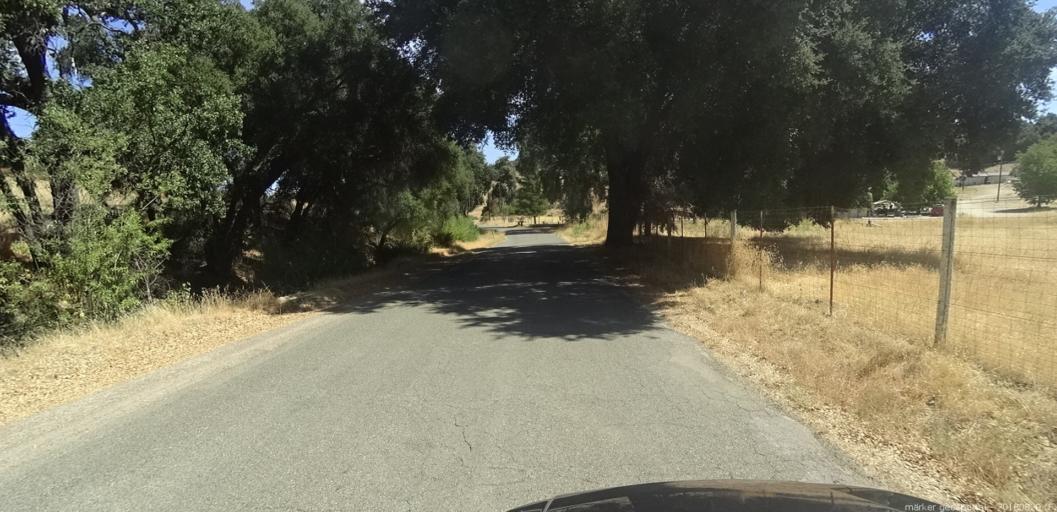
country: US
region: California
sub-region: San Luis Obispo County
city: Lake Nacimiento
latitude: 35.8364
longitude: -121.0414
